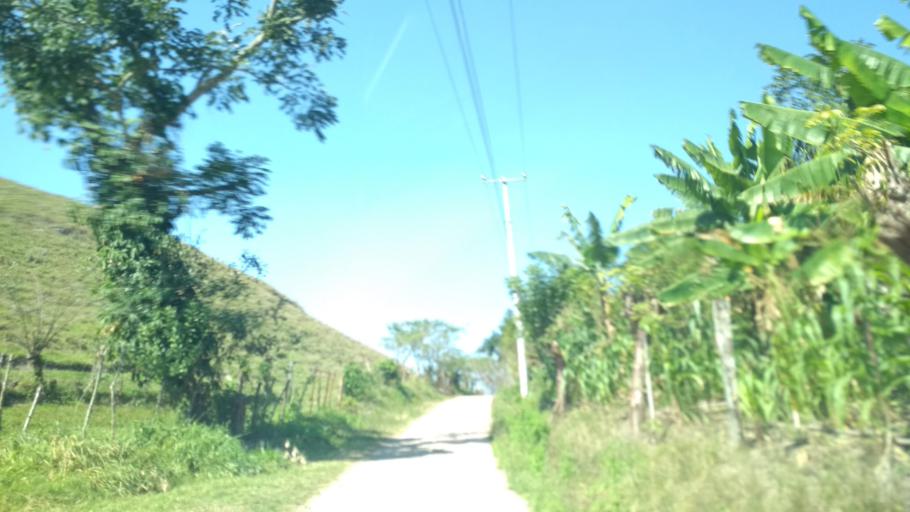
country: MX
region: Veracruz
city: Gutierrez Zamora
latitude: 20.4892
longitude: -97.1645
